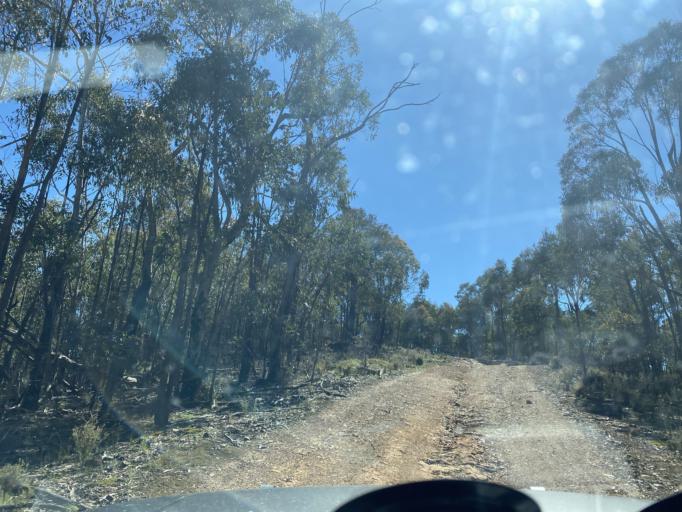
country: AU
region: Victoria
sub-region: Benalla
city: Benalla
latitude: -36.7275
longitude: 146.1825
